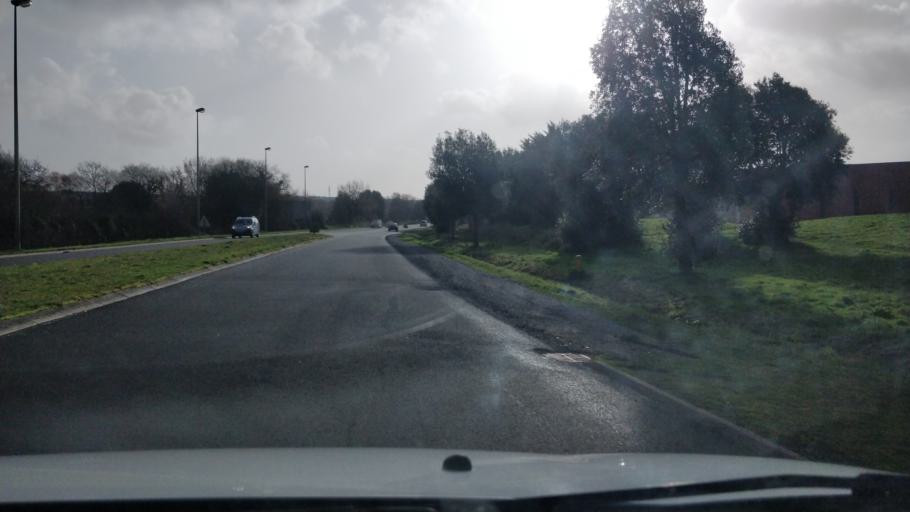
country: FR
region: Pays de la Loire
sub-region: Departement de la Loire-Atlantique
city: Guerande
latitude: 47.3326
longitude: -2.4186
